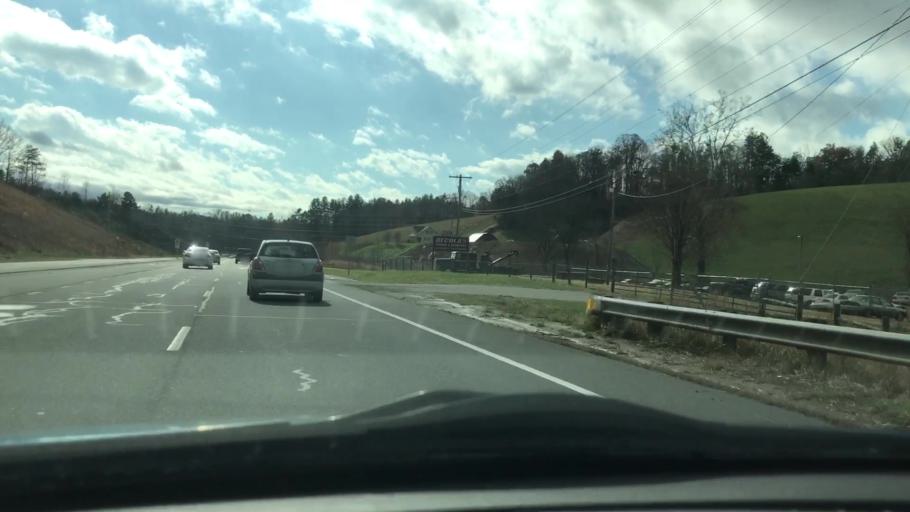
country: US
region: North Carolina
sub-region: Madison County
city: Mars Hill
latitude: 35.8631
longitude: -82.4851
